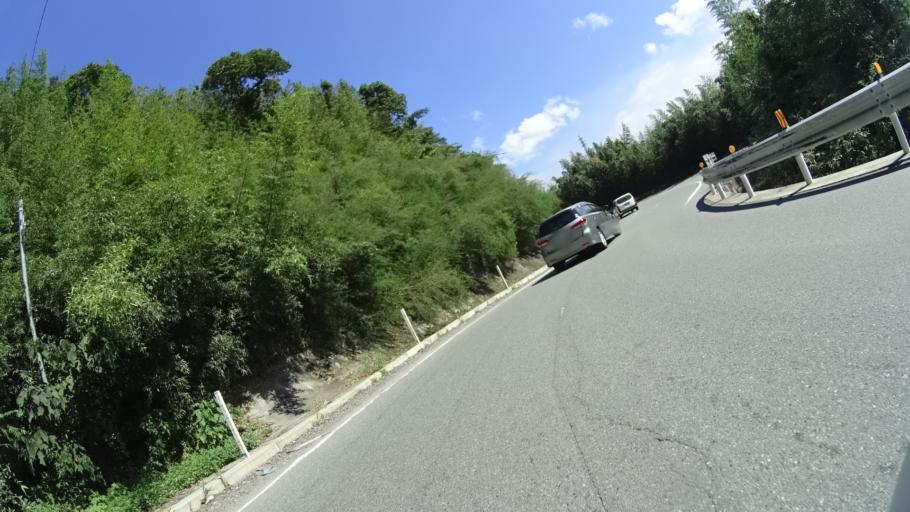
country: JP
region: Kumamoto
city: Aso
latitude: 32.8889
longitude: 130.9941
